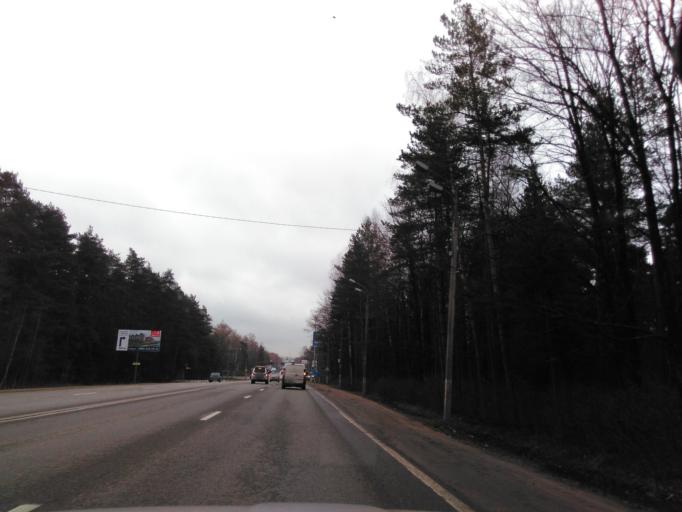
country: RU
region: Moskovskaya
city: Opalikha
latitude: 55.8410
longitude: 37.2175
